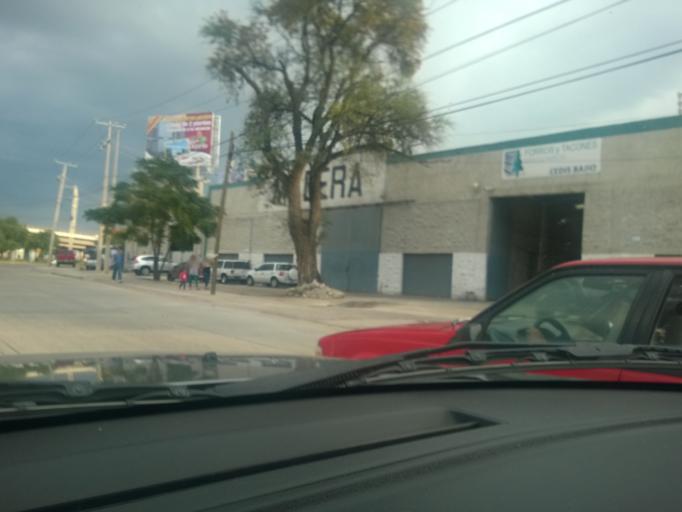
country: MX
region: Guanajuato
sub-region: Leon
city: Medina
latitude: 21.1148
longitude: -101.6270
